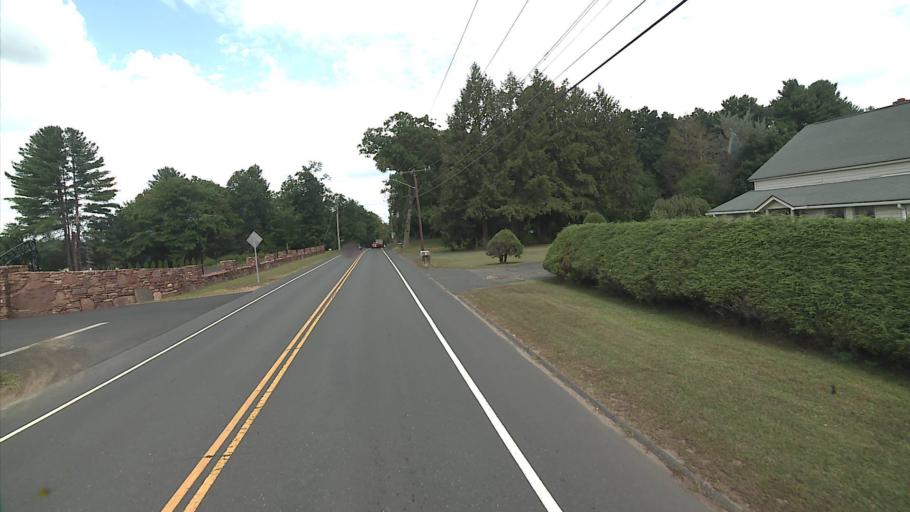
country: US
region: Connecticut
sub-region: Hartford County
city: Salmon Brook
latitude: 41.9418
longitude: -72.7764
